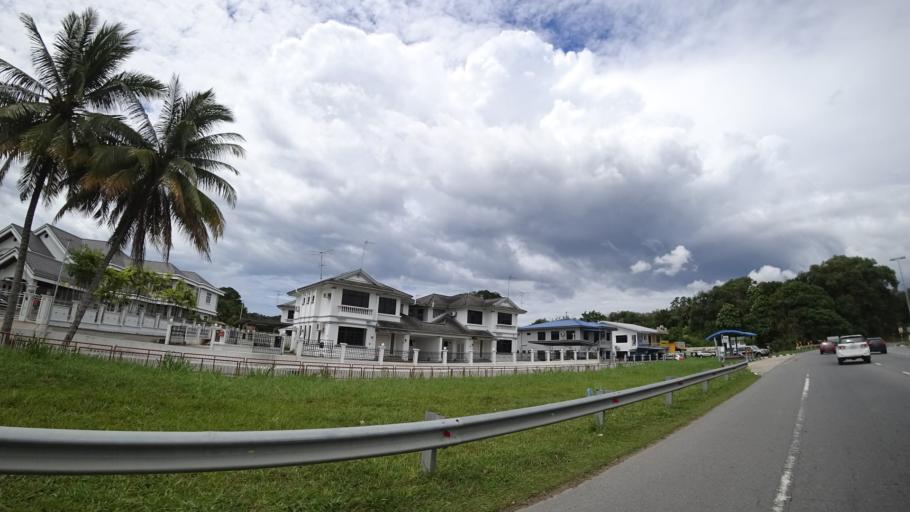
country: BN
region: Brunei and Muara
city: Bandar Seri Begawan
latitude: 4.8795
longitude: 114.8706
